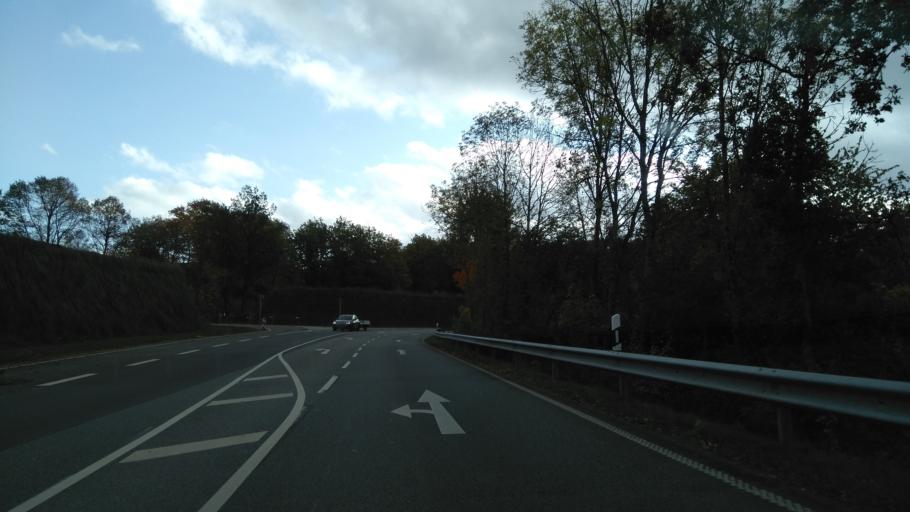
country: DE
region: Rheinland-Pfalz
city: Trier
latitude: 49.7159
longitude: 6.6296
